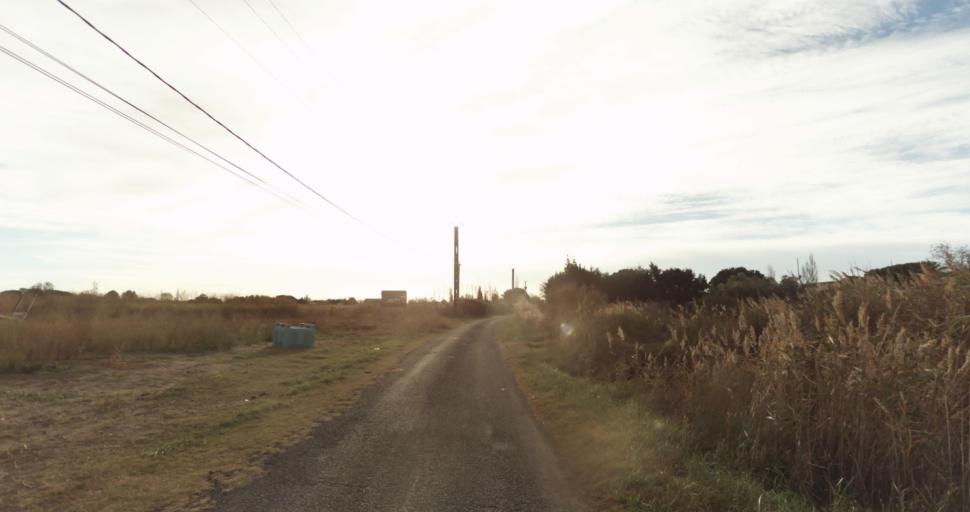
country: FR
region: Languedoc-Roussillon
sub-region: Departement du Gard
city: Aigues-Mortes
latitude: 43.5558
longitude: 4.2111
